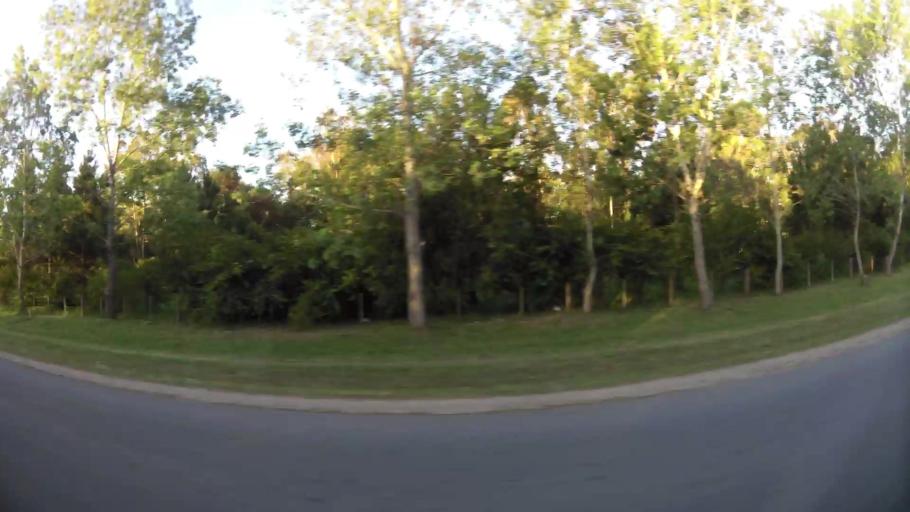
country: UY
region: Canelones
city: Barra de Carrasco
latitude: -34.8453
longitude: -56.0087
